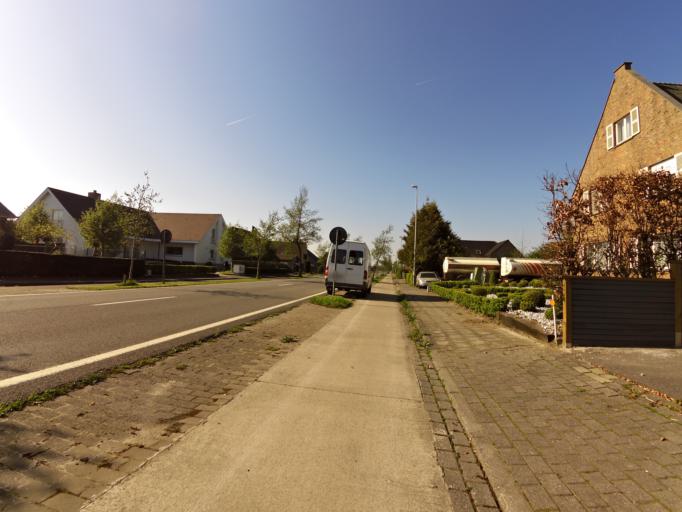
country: BE
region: Flanders
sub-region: Provincie West-Vlaanderen
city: Oudenburg
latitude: 51.1685
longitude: 3.0131
